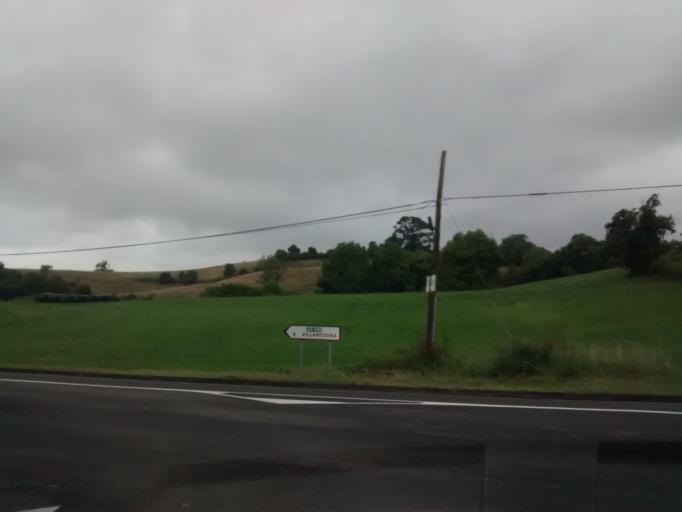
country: ES
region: Asturias
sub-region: Province of Asturias
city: Villaviciosa
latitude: 43.5008
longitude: -5.4267
